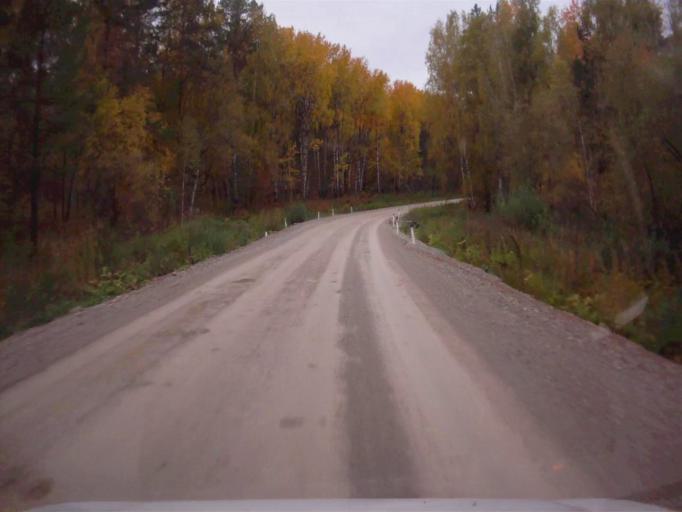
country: RU
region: Chelyabinsk
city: Nyazepetrovsk
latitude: 56.0685
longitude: 59.4334
